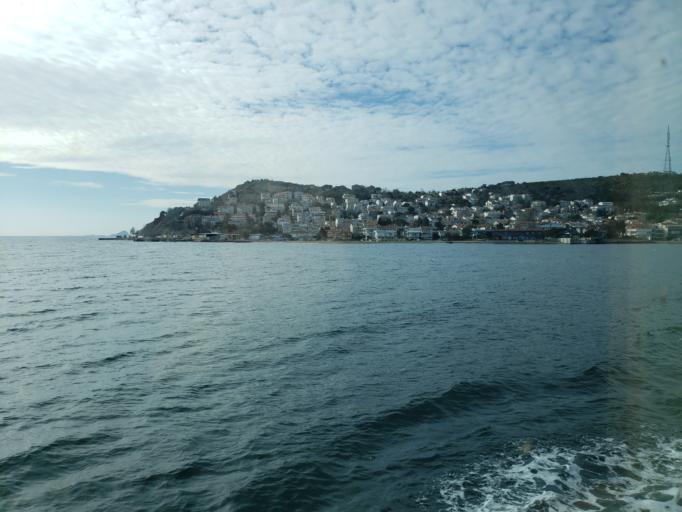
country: TR
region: Istanbul
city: Kinali
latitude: 40.9057
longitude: 29.0605
